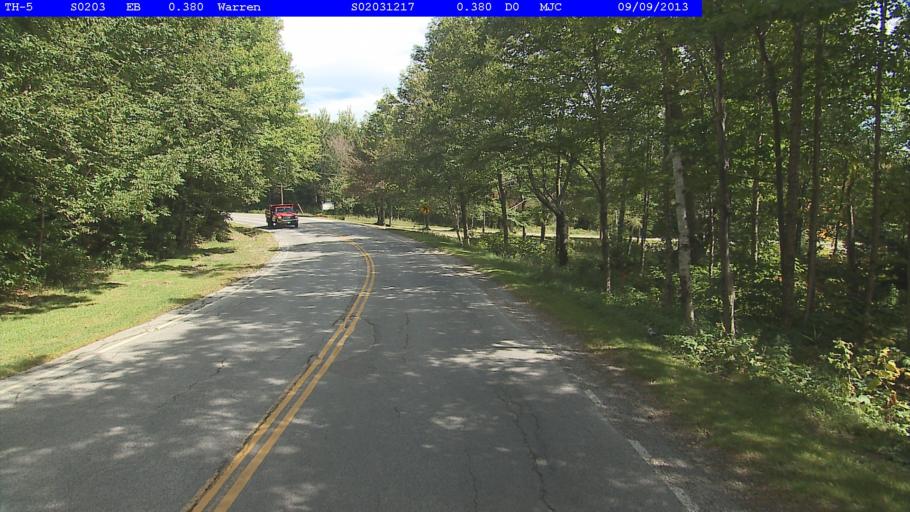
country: US
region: Vermont
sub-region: Addison County
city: Bristol
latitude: 44.1370
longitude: -72.8880
